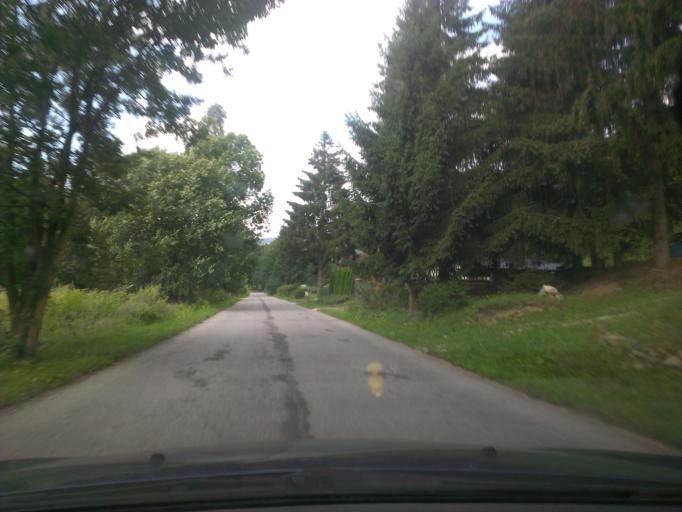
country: SK
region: Zilinsky
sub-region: Okres Zilina
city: Vrutky
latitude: 49.1049
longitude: 18.8894
